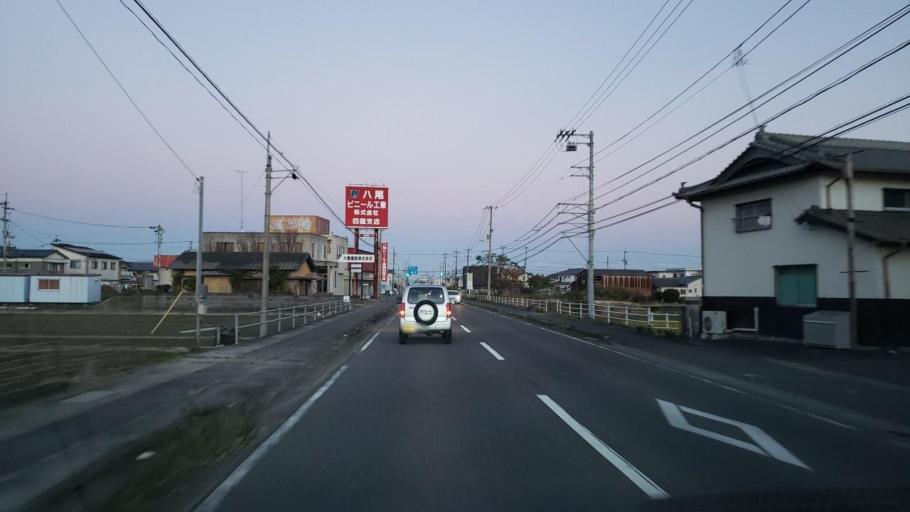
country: JP
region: Tokushima
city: Ishii
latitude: 34.1215
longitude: 134.4479
